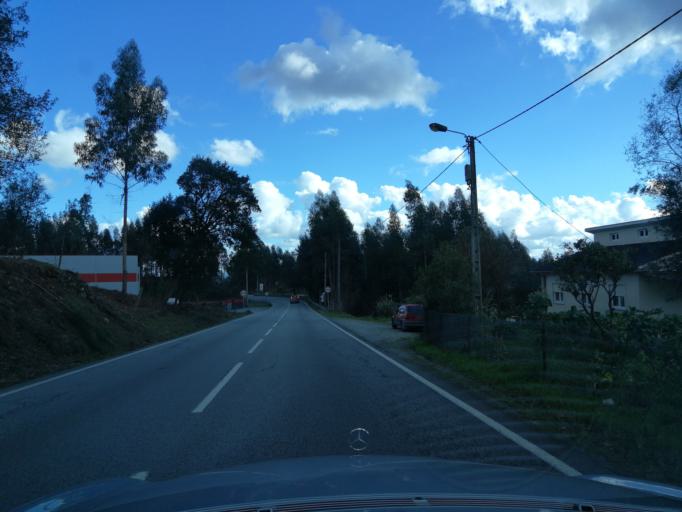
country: PT
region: Braga
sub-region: Vila Verde
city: Prado
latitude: 41.6594
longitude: -8.5193
